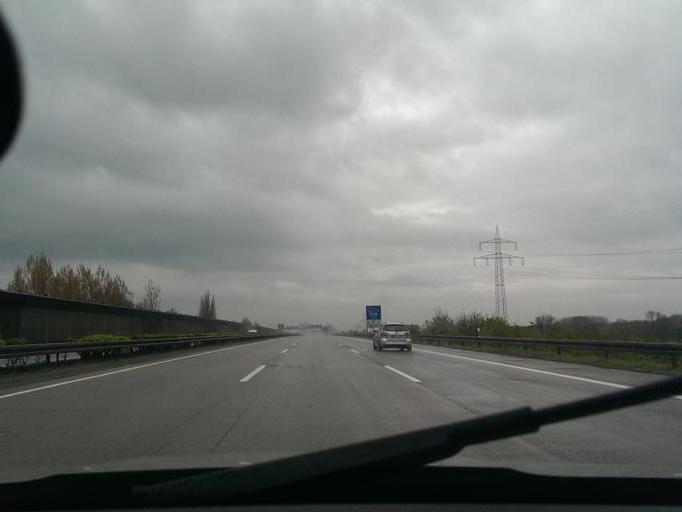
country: DE
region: Lower Saxony
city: Lehrte
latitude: 52.3793
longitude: 9.8972
